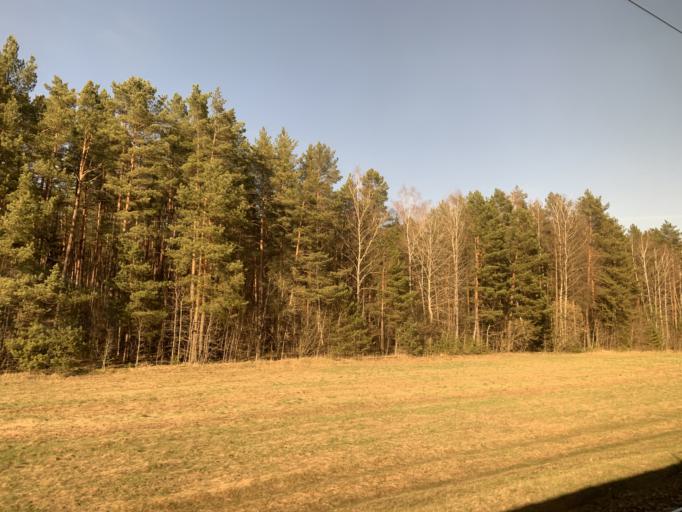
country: BY
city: Soly
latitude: 54.4915
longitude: 26.2918
